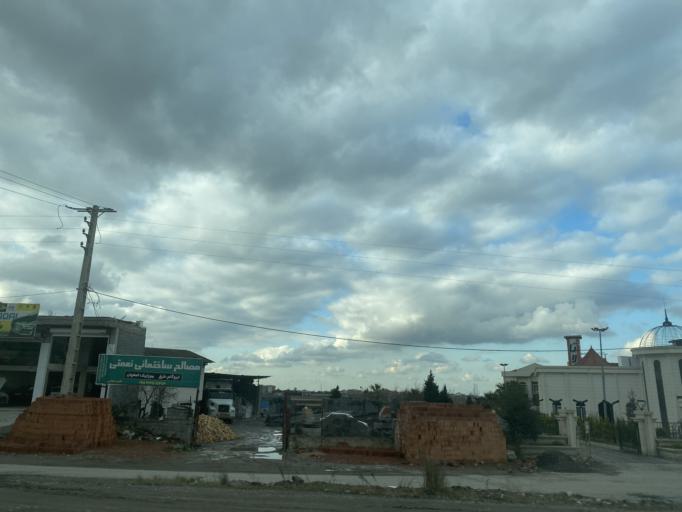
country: IR
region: Mazandaran
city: Amol
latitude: 36.4436
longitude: 52.3847
